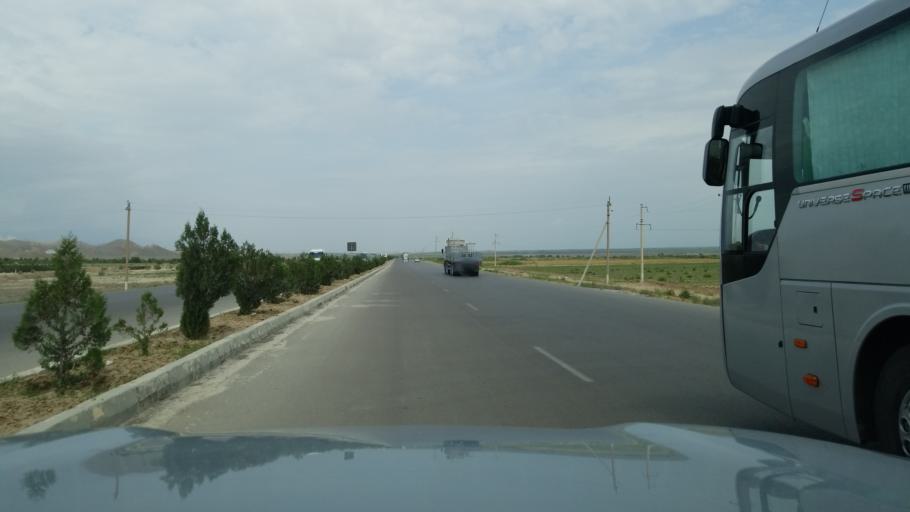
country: TM
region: Ahal
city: Baharly
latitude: 38.2368
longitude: 57.7744
